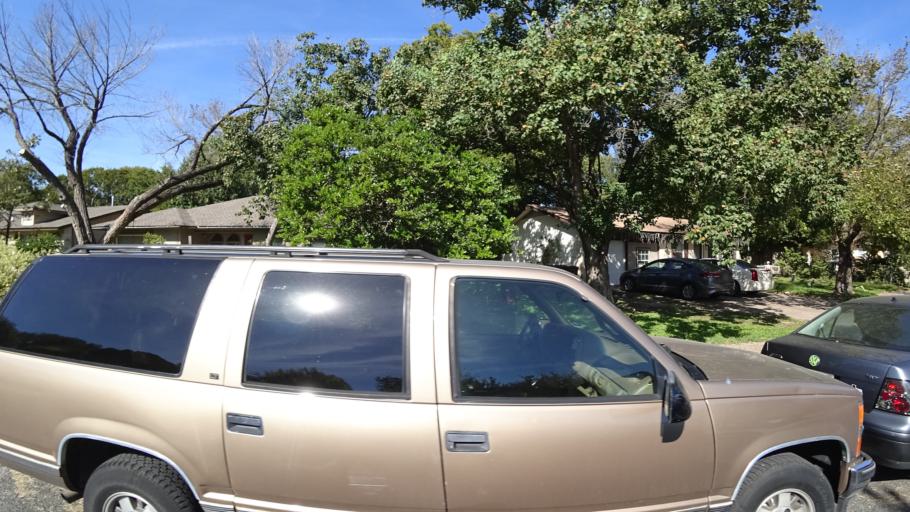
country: US
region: Texas
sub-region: Travis County
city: Austin
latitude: 30.1983
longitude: -97.7513
